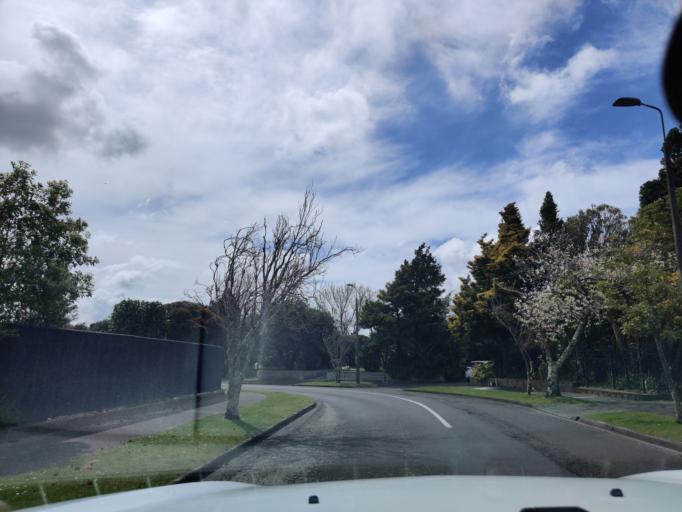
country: NZ
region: Manawatu-Wanganui
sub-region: Palmerston North City
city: Palmerston North
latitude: -40.3791
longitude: 175.5974
